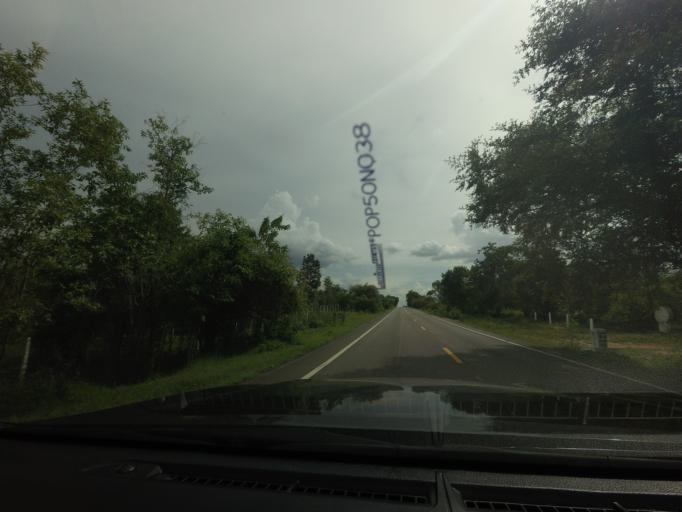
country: TH
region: Kanchanaburi
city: Kanchanaburi
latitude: 14.1518
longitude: 99.4228
